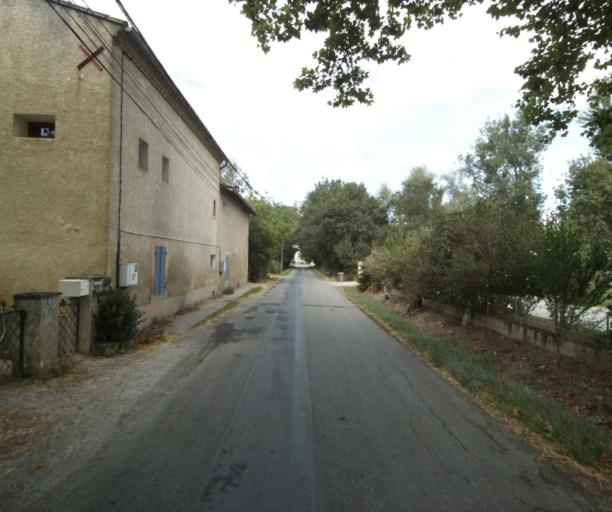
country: FR
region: Midi-Pyrenees
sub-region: Departement de la Haute-Garonne
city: Revel
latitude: 43.4682
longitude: 2.0014
